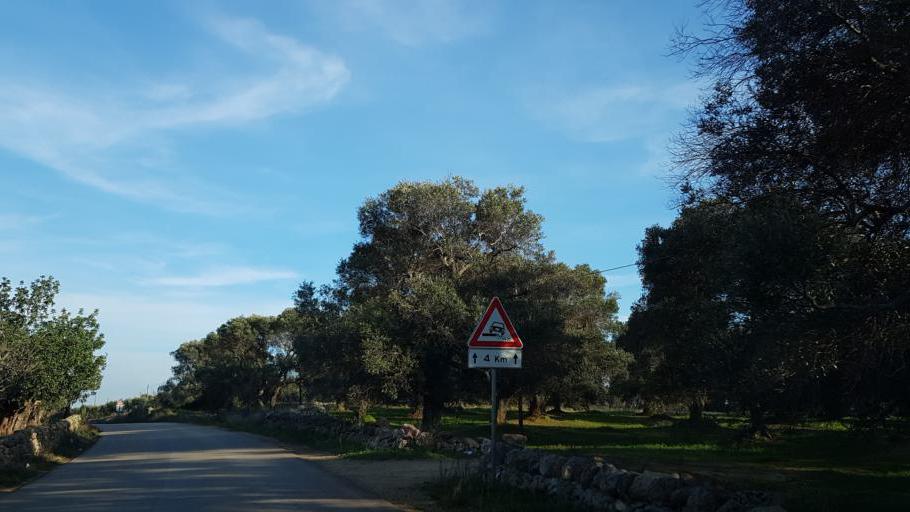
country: IT
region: Apulia
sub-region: Provincia di Brindisi
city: San Vito dei Normanni
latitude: 40.7007
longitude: 17.7297
